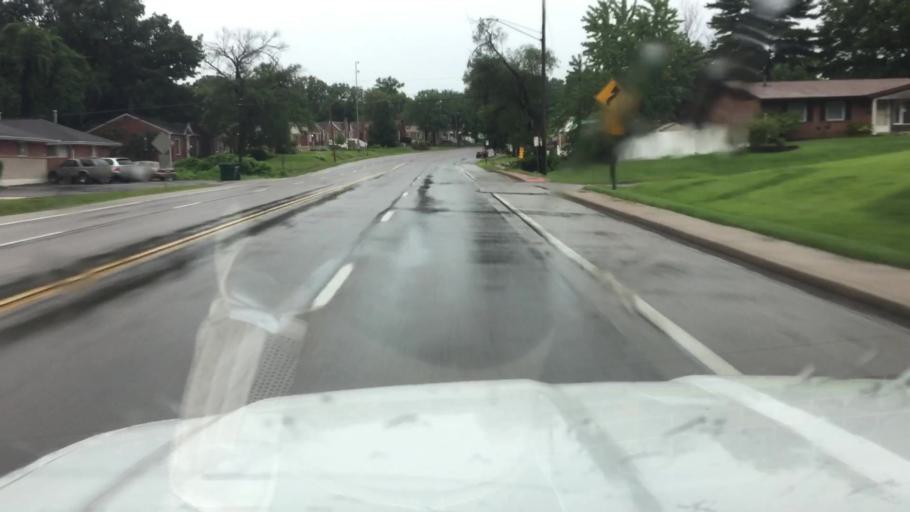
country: US
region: Missouri
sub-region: Saint Louis County
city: Lemay
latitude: 38.5154
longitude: -90.2844
